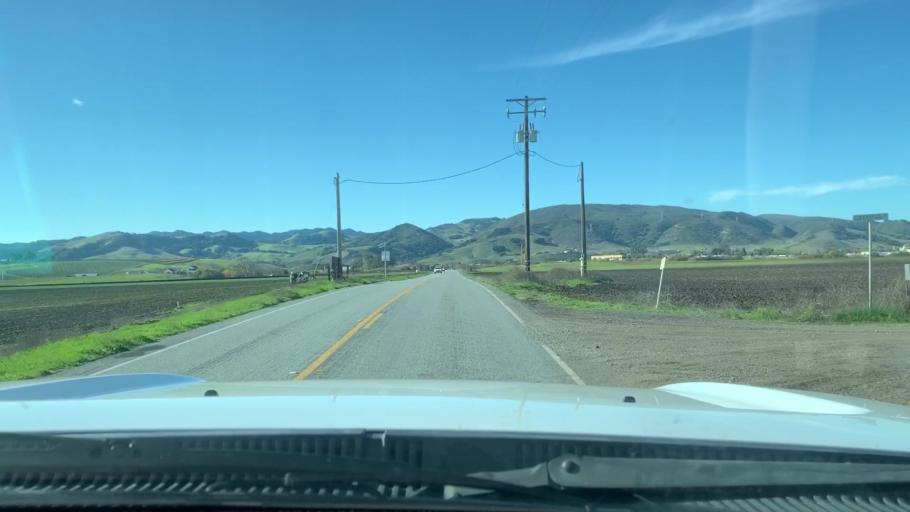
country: US
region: California
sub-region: San Luis Obispo County
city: San Luis Obispo
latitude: 35.2360
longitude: -120.6601
